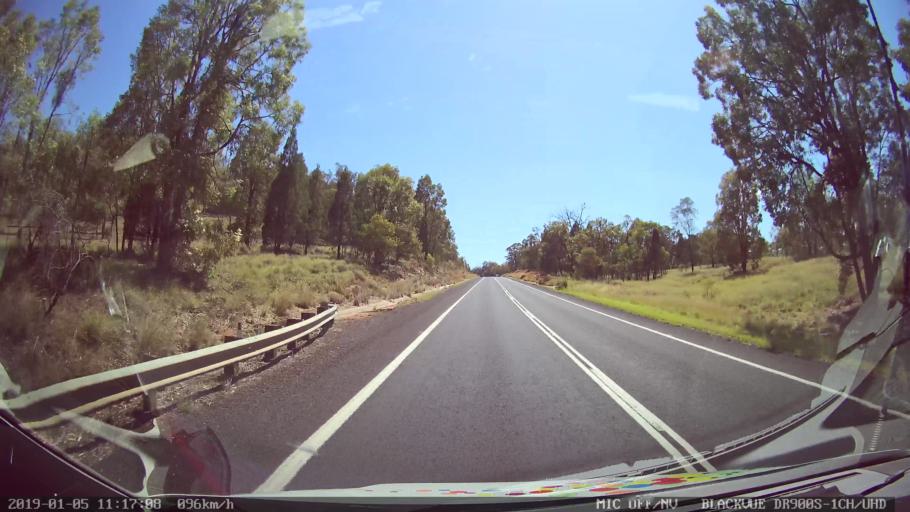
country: AU
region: New South Wales
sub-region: Warrumbungle Shire
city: Coonabarabran
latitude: -31.3297
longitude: 149.3037
